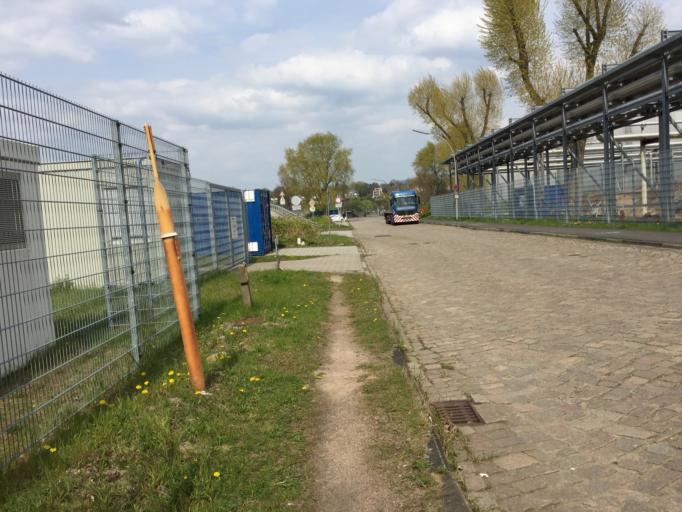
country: DE
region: Hamburg
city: Altona
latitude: 53.5381
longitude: 9.8845
